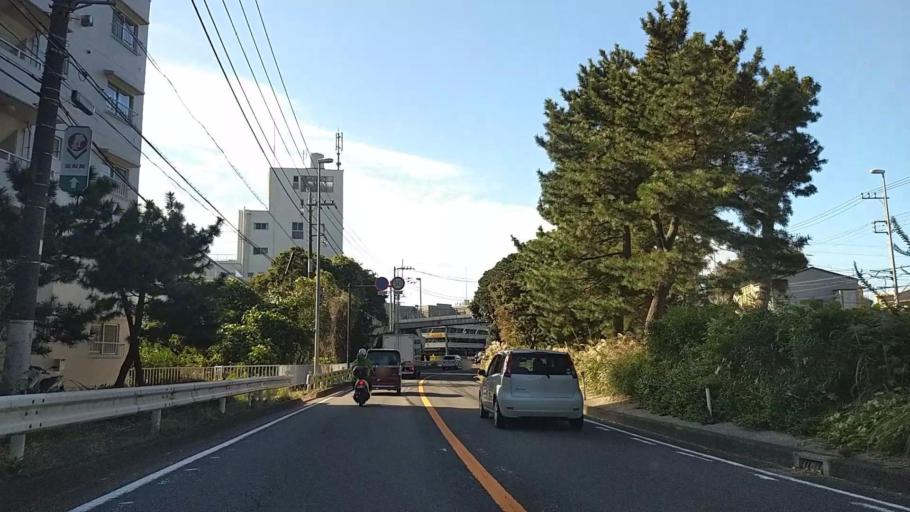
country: JP
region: Kanagawa
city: Fujisawa
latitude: 35.3855
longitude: 139.5170
